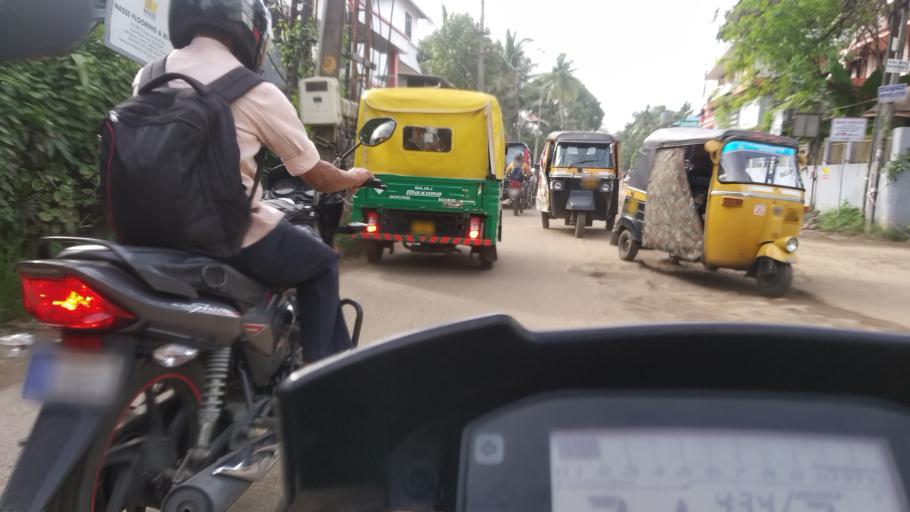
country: IN
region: Kerala
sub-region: Ernakulam
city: Cochin
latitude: 9.9801
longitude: 76.3136
